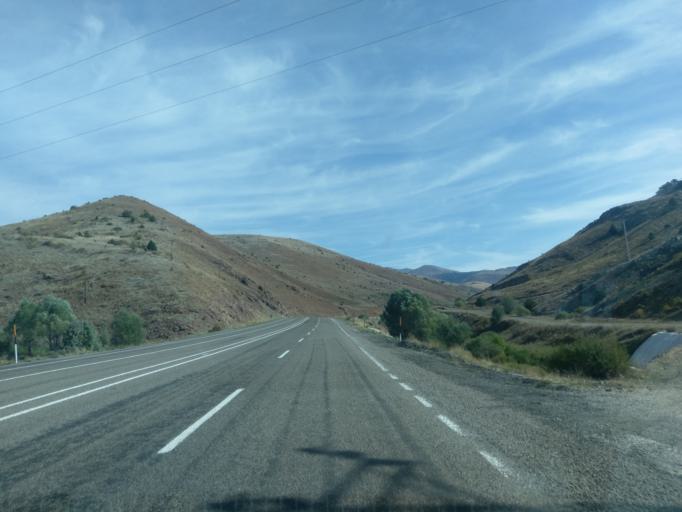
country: TR
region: Sivas
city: Imranli
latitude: 39.8516
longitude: 38.2961
